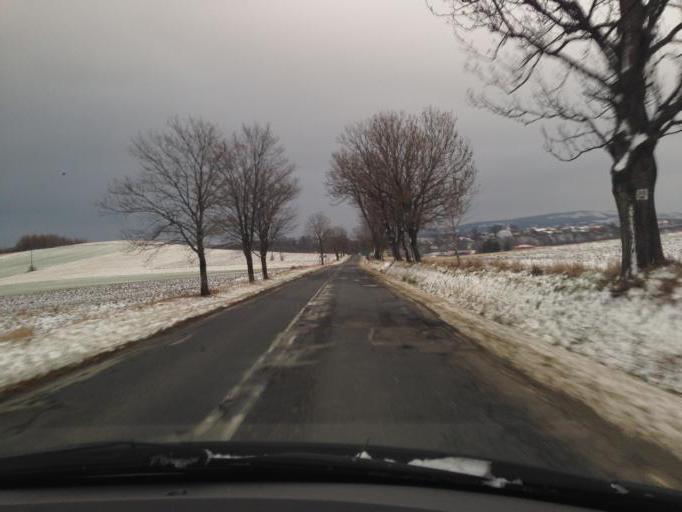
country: PL
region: Subcarpathian Voivodeship
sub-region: Powiat jasielski
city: Nowy Zmigrod
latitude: 49.6094
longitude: 21.5080
